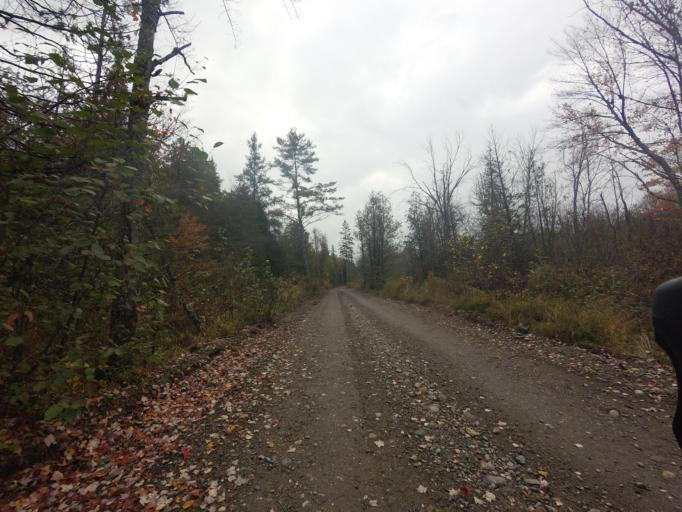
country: CA
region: Ontario
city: Renfrew
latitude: 45.1726
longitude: -76.6811
